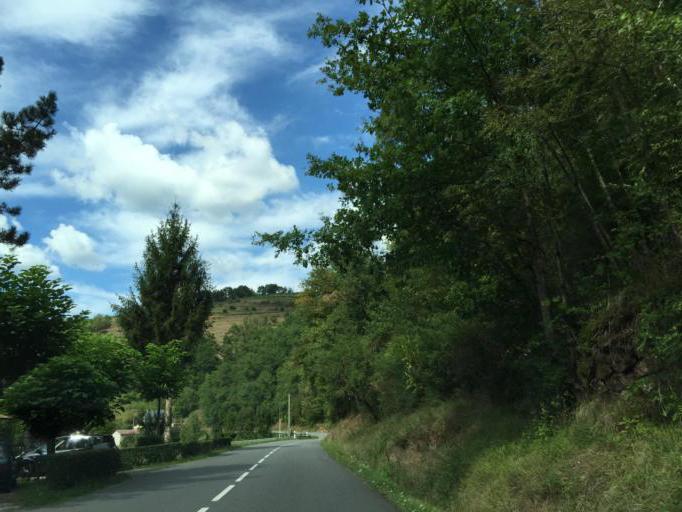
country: FR
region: Midi-Pyrenees
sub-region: Departement de l'Aveyron
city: Saint-Christophe-Vallon
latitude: 44.5016
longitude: 2.4343
